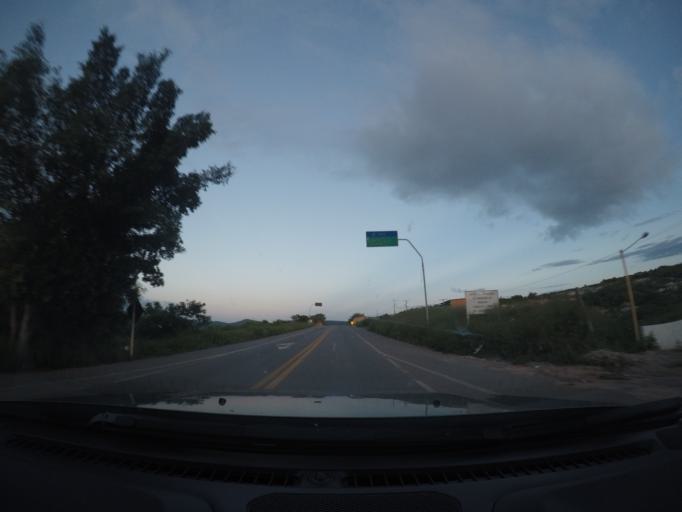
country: BR
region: Bahia
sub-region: Seabra
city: Seabra
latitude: -12.4271
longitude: -41.7677
